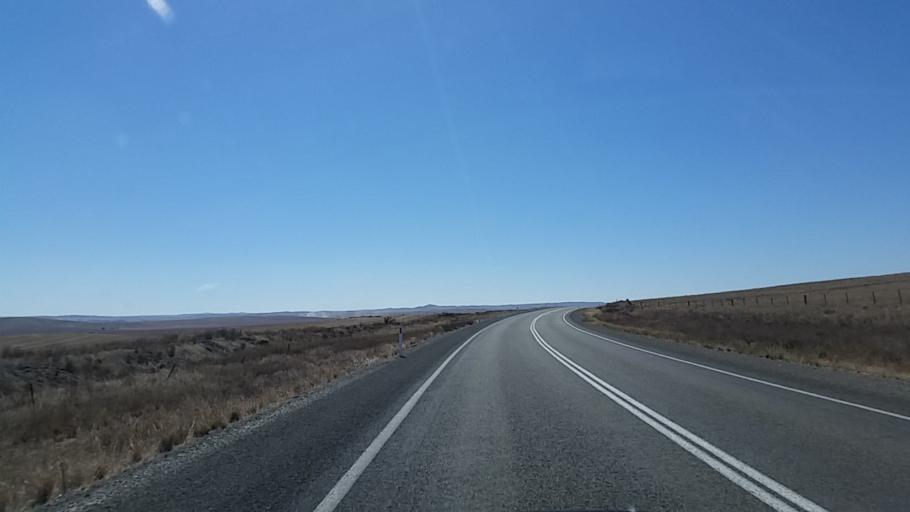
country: AU
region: South Australia
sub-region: Northern Areas
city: Jamestown
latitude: -33.3233
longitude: 138.8844
